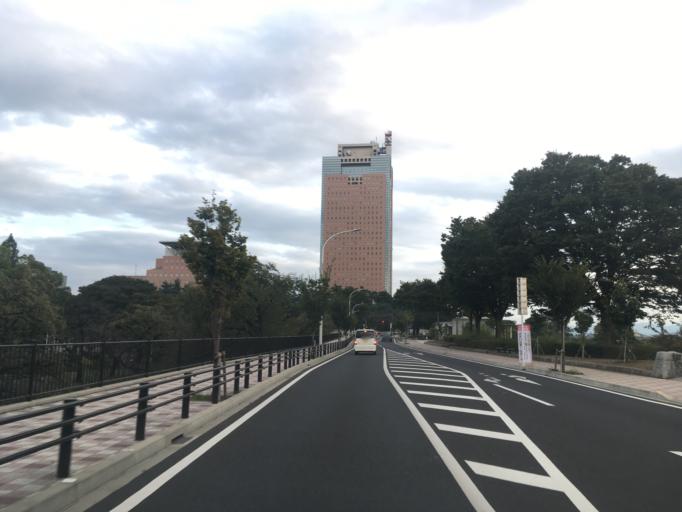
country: JP
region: Gunma
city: Maebashi-shi
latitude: 36.3949
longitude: 139.0594
